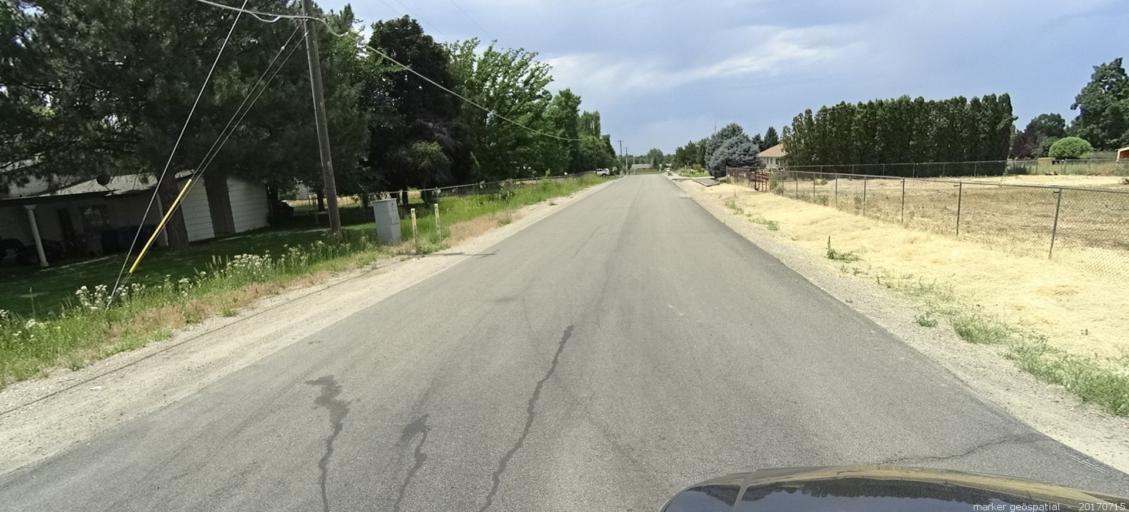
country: US
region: Idaho
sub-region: Ada County
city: Garden City
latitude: 43.5694
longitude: -116.3042
